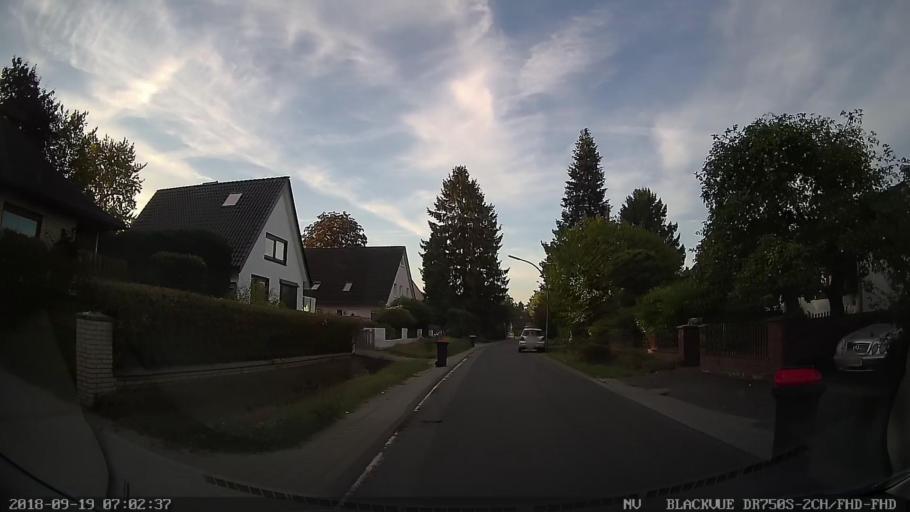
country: DE
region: Hamburg
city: Eidelstedt
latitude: 53.6265
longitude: 9.9010
